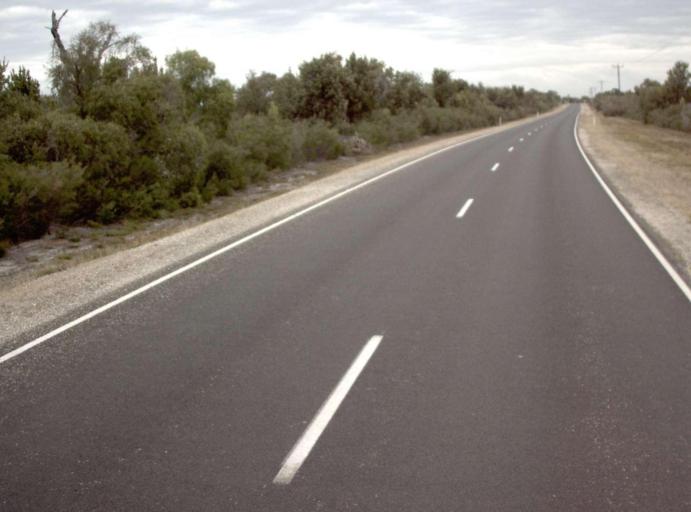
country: AU
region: Victoria
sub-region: Wellington
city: Sale
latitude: -38.1937
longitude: 147.3643
